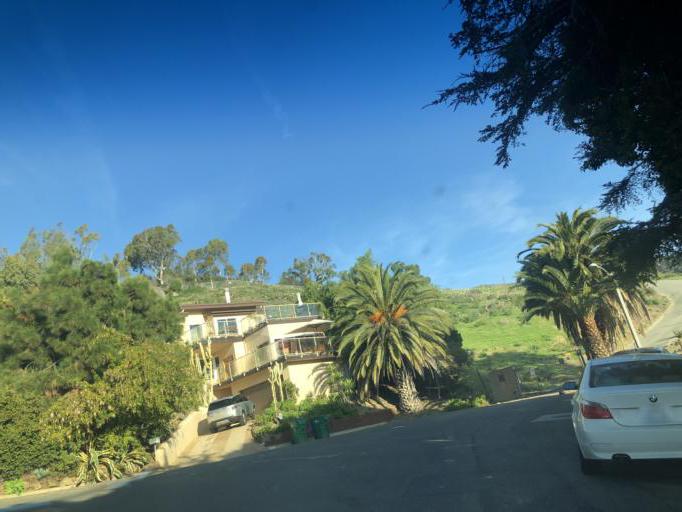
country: US
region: California
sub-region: Orange County
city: Laguna Beach
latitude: 33.5493
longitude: -117.7851
